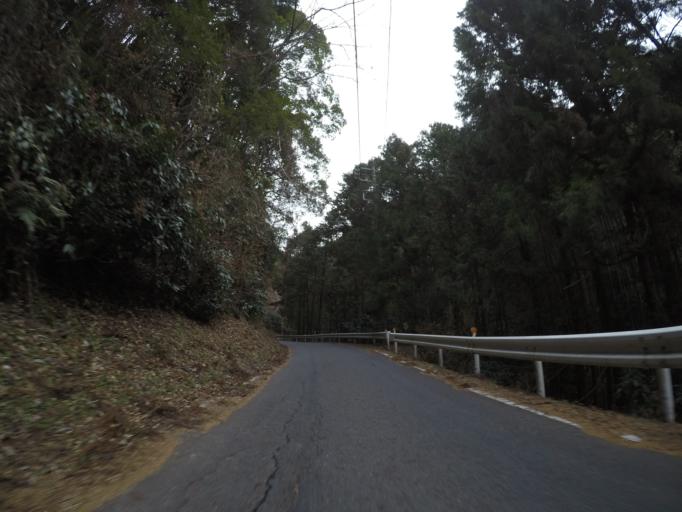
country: JP
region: Shizuoka
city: Fujinomiya
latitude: 35.2576
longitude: 138.5406
